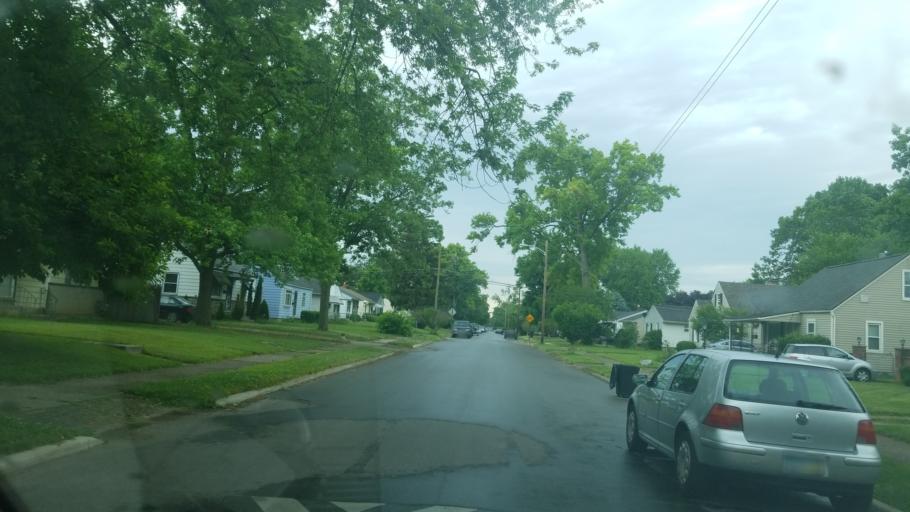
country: US
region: Ohio
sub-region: Franklin County
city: Minerva Park
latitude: 40.0291
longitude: -82.9879
